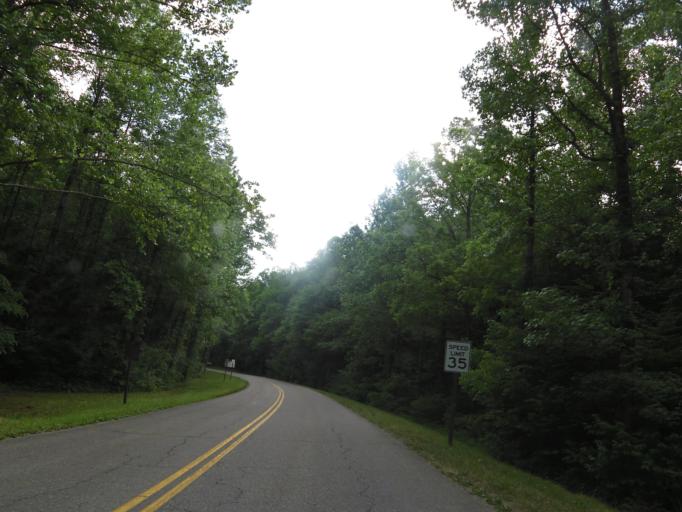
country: US
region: Tennessee
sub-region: Sevier County
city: Gatlinburg
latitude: 35.6865
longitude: -83.5408
